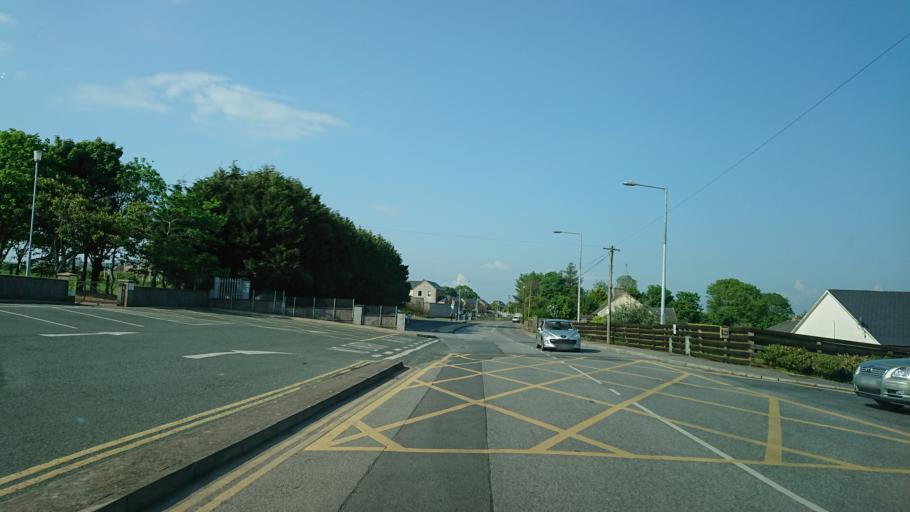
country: IE
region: Munster
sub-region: Waterford
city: Waterford
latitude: 52.2259
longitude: -7.0645
